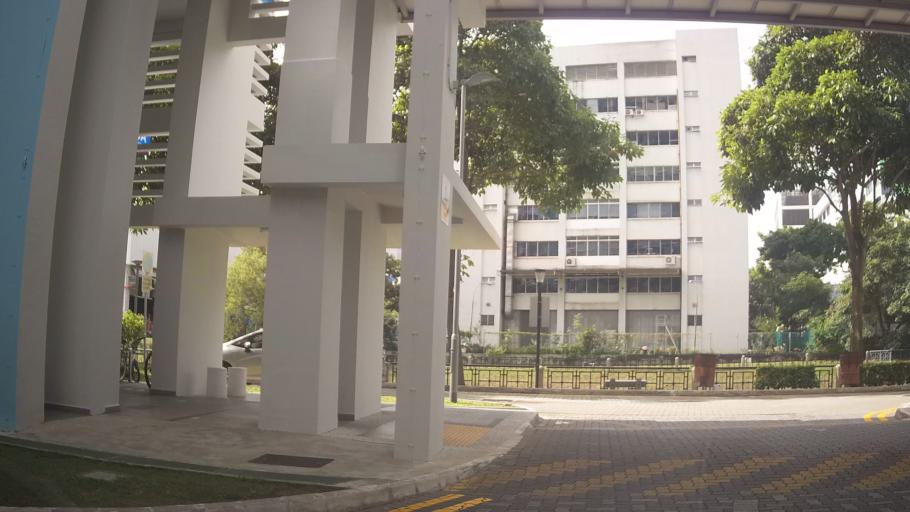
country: SG
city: Singapore
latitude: 1.3204
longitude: 103.8666
